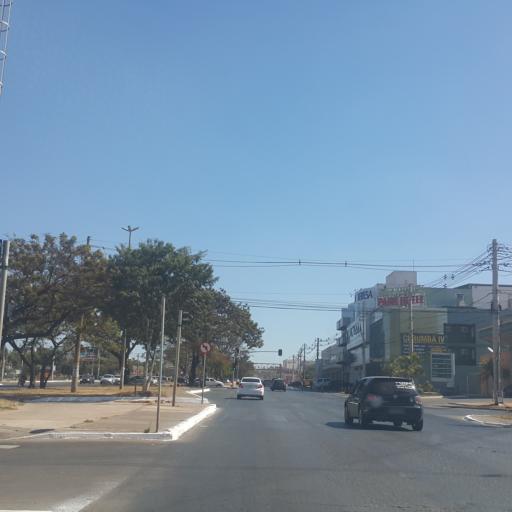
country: BR
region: Federal District
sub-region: Brasilia
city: Brasilia
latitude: -15.8079
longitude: -48.0832
